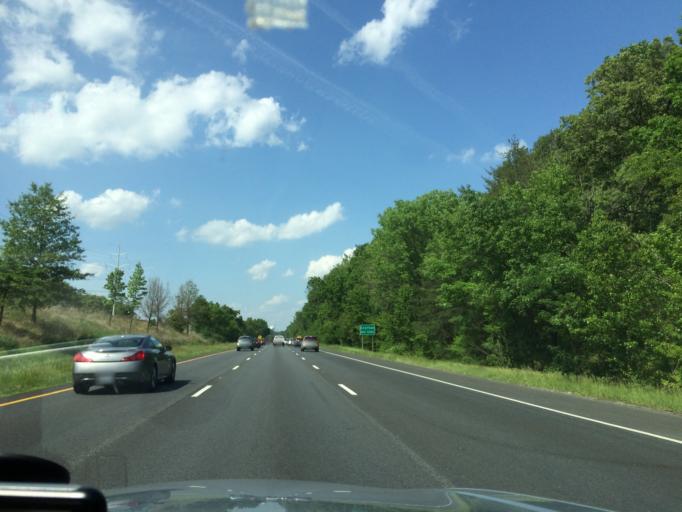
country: US
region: Maryland
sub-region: Anne Arundel County
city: Crofton
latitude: 39.0045
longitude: -76.6992
